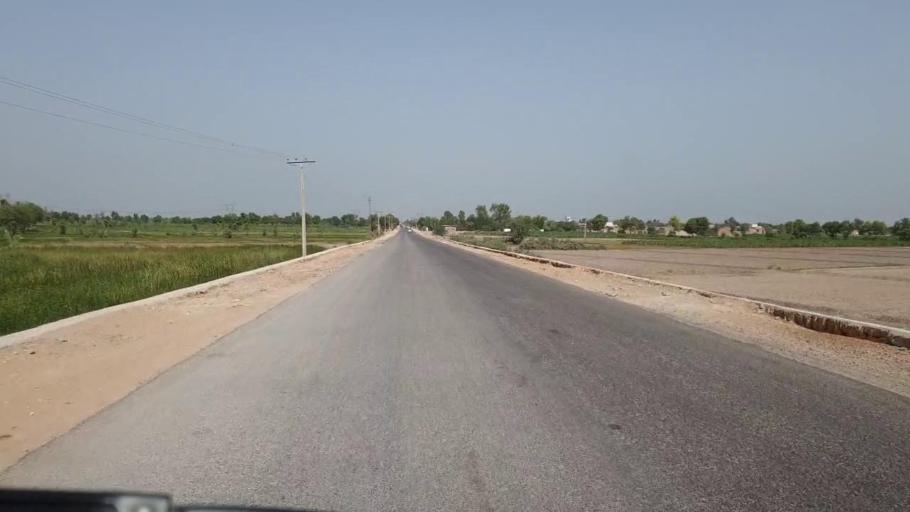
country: PK
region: Sindh
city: Sakrand
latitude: 26.2599
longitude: 68.1868
